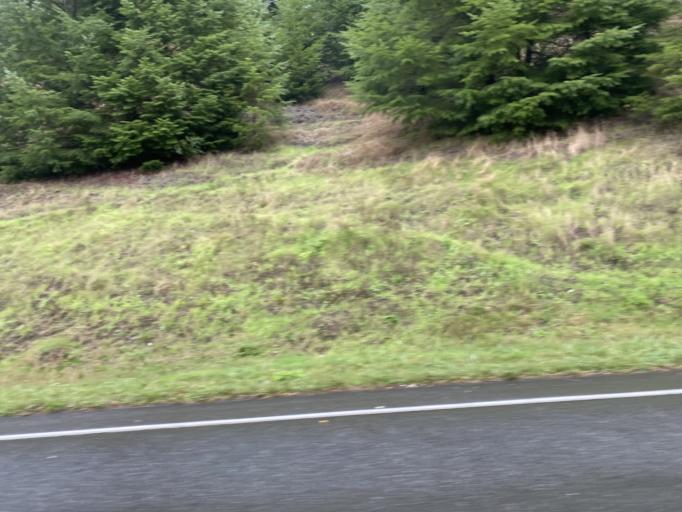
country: US
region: Washington
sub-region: Island County
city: Langley
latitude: 48.0542
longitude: -122.4522
